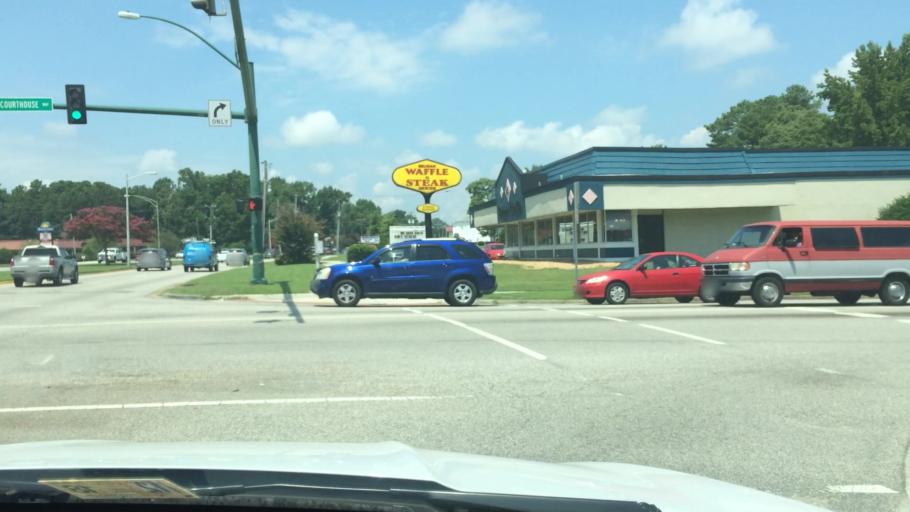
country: US
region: Virginia
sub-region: York County
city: Yorktown
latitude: 37.1327
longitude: -76.5421
